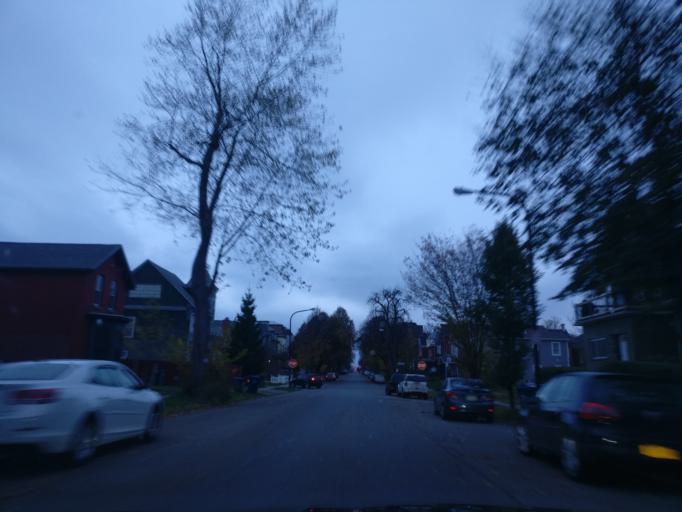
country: US
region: New York
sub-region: Erie County
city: Buffalo
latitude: 42.8982
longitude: -78.8876
